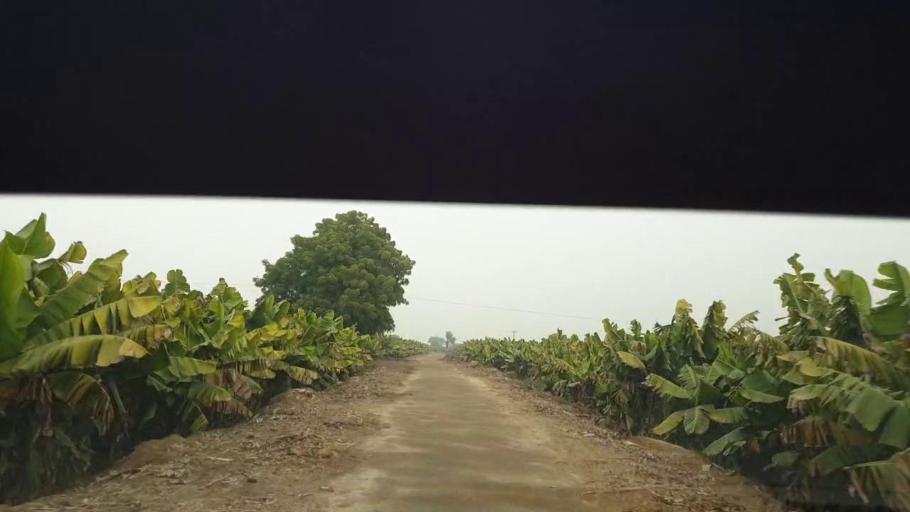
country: PK
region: Sindh
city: Berani
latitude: 25.7804
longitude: 68.7333
